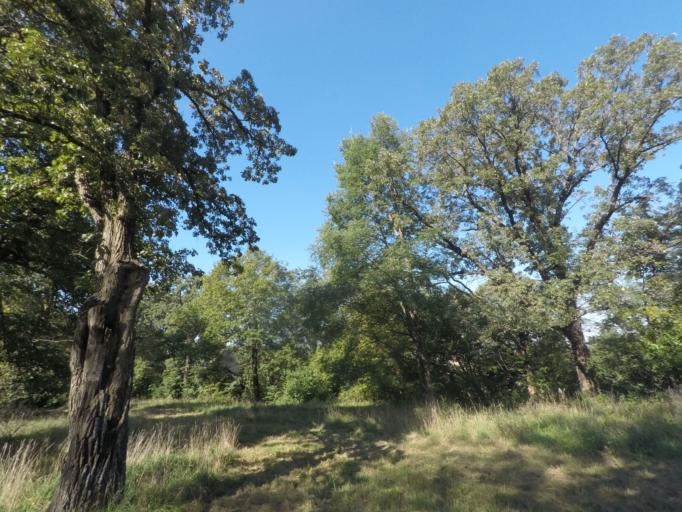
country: US
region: Iowa
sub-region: Story County
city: Nevada
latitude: 42.0339
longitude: -93.3733
